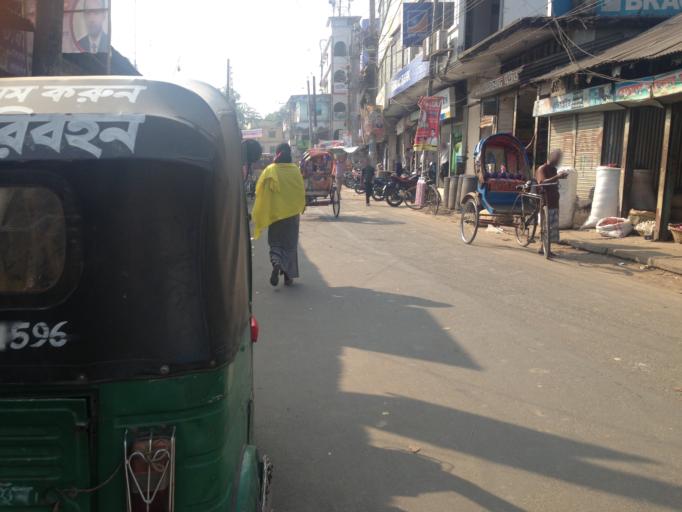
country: BD
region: Chittagong
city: Lakshmipur
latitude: 22.9369
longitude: 90.8286
